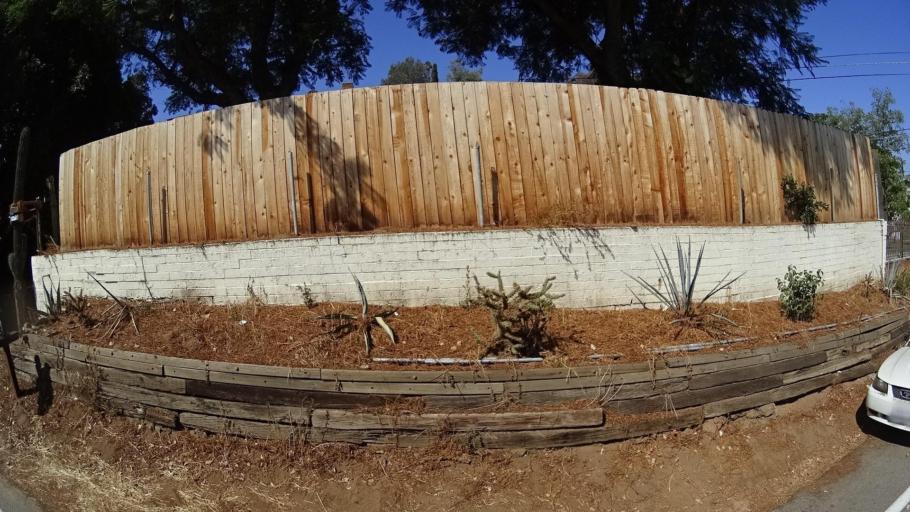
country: US
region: California
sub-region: San Diego County
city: Lakeside
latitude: 32.8499
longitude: -116.9355
